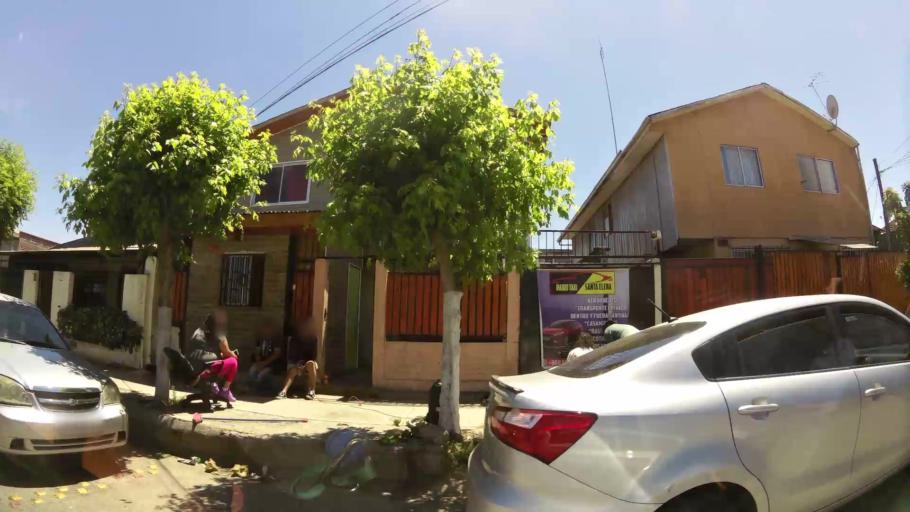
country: CL
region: Santiago Metropolitan
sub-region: Provincia de Santiago
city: La Pintana
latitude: -33.5682
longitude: -70.6619
